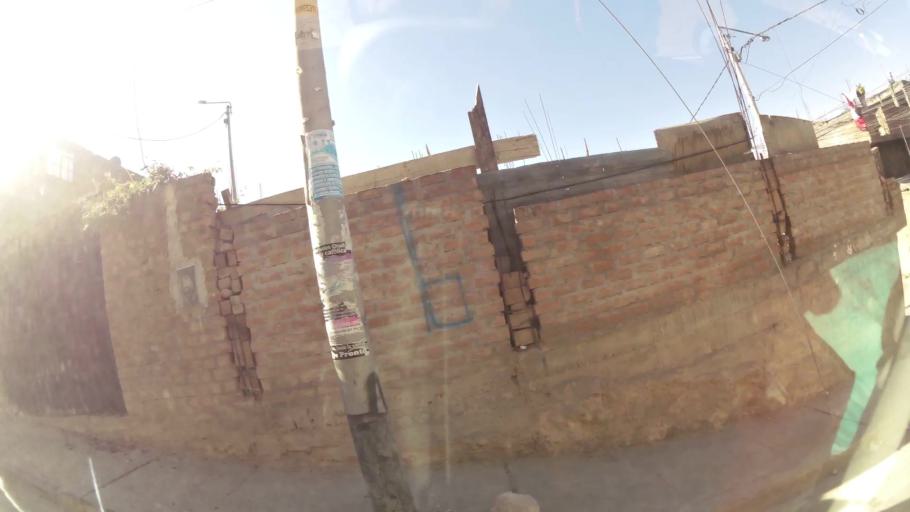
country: PE
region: Ayacucho
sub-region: Provincia de Huamanga
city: Ayacucho
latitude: -13.1651
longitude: -74.2347
